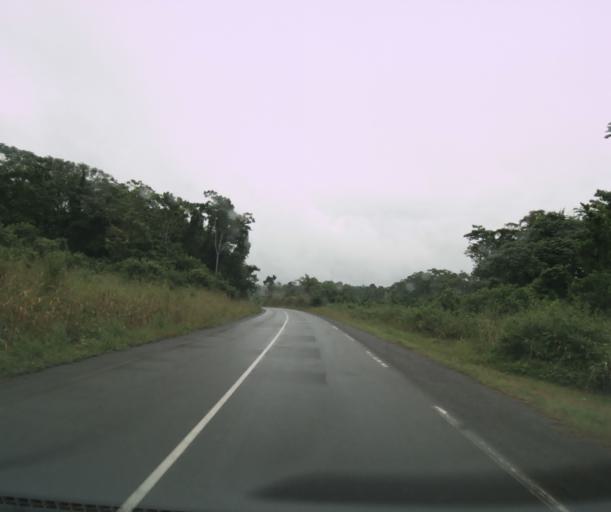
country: CM
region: Littoral
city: Dizangue
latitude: 3.3658
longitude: 10.1026
